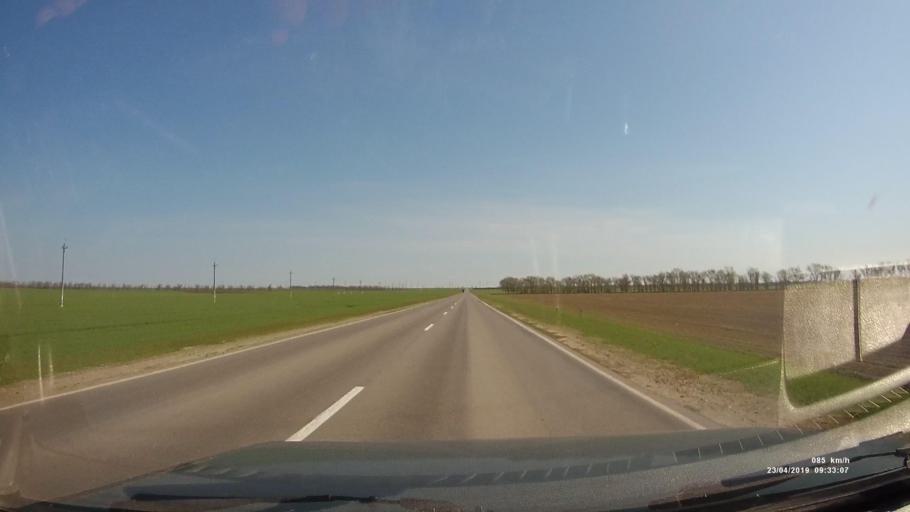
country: RU
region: Rostov
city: Gundorovskiy
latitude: 46.7974
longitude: 41.8436
